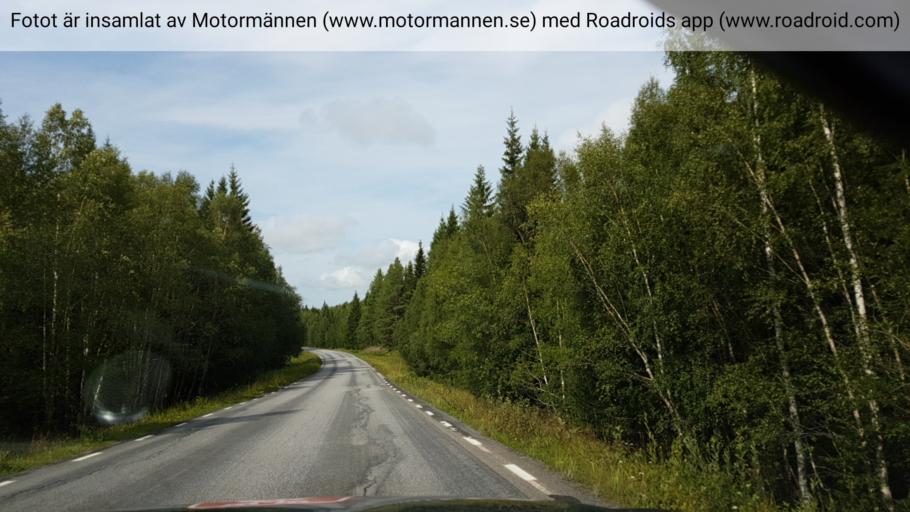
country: SE
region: Jaemtland
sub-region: Krokoms Kommun
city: Krokom
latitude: 63.2708
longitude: 14.3743
